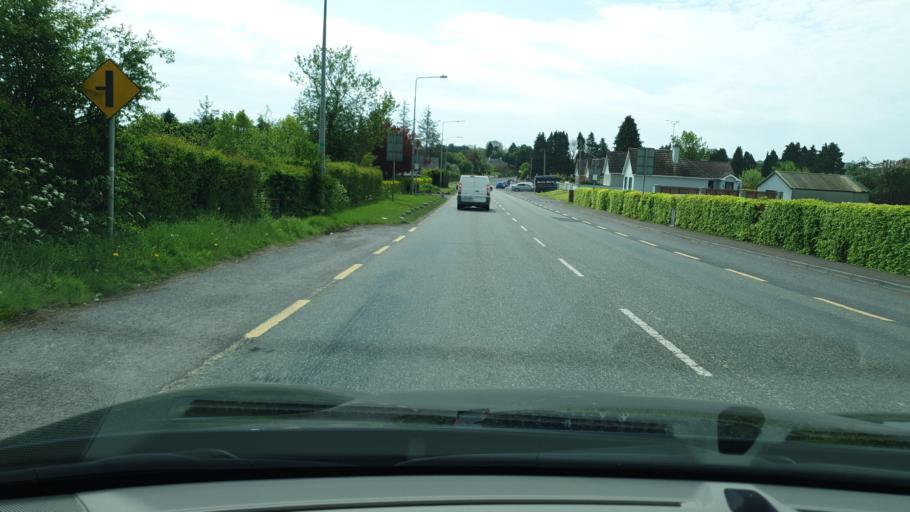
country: IE
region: Ulster
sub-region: An Cabhan
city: Kingscourt
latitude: 53.8173
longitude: -6.7407
